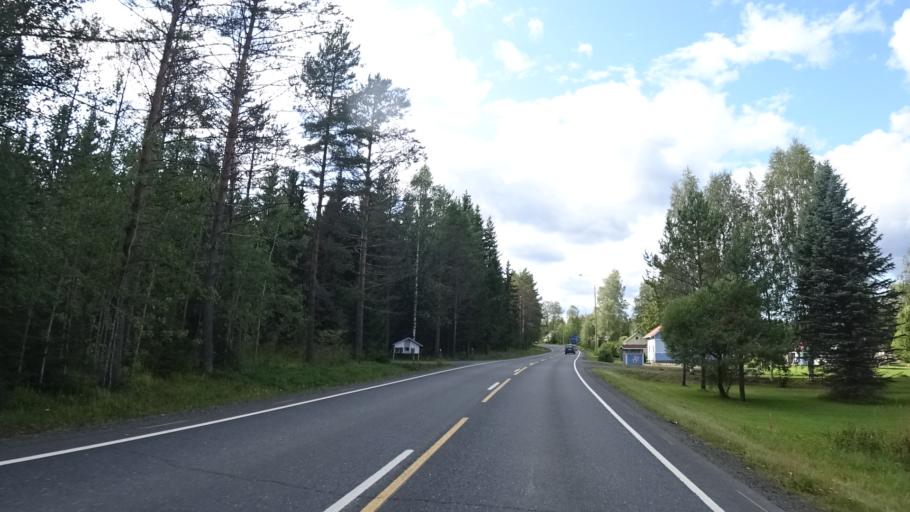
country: FI
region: North Karelia
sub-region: Keski-Karjala
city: Tohmajaervi
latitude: 62.1888
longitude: 30.4590
